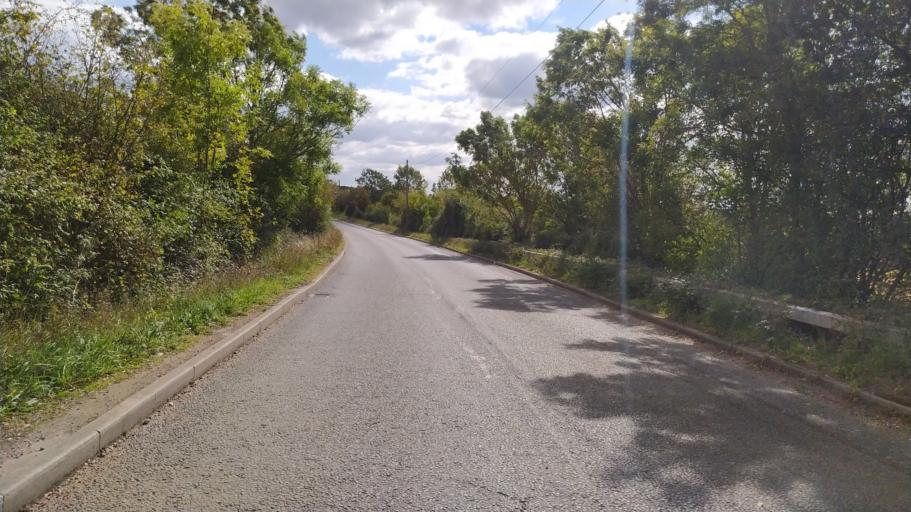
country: GB
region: England
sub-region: Reading
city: Reading
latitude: 51.4175
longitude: -0.9953
